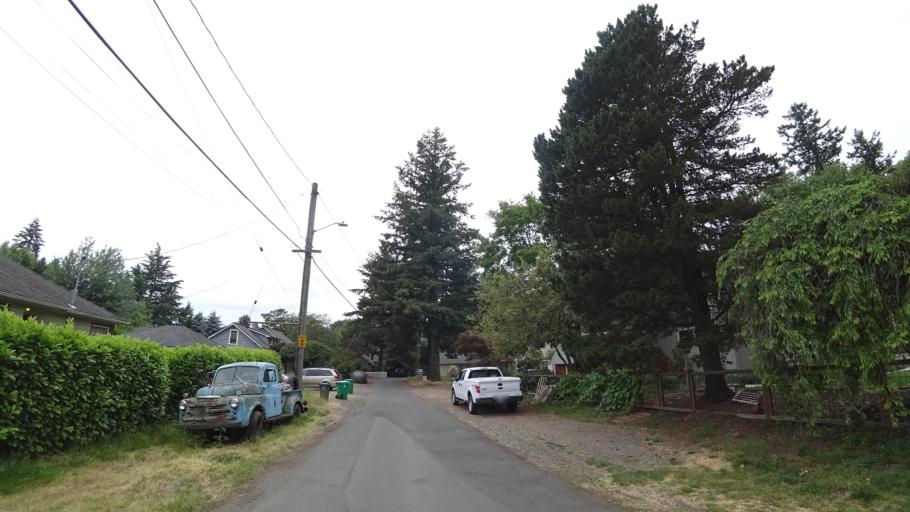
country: US
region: Oregon
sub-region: Multnomah County
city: Lents
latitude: 45.5079
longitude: -122.5854
